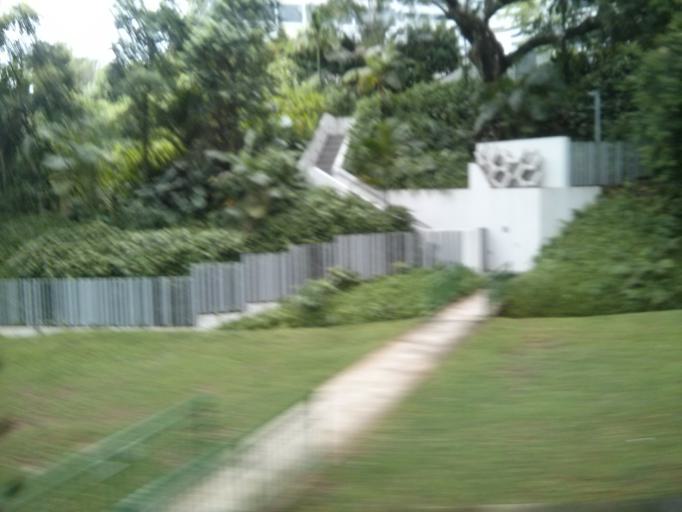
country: SG
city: Singapore
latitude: 1.2834
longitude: 103.8014
